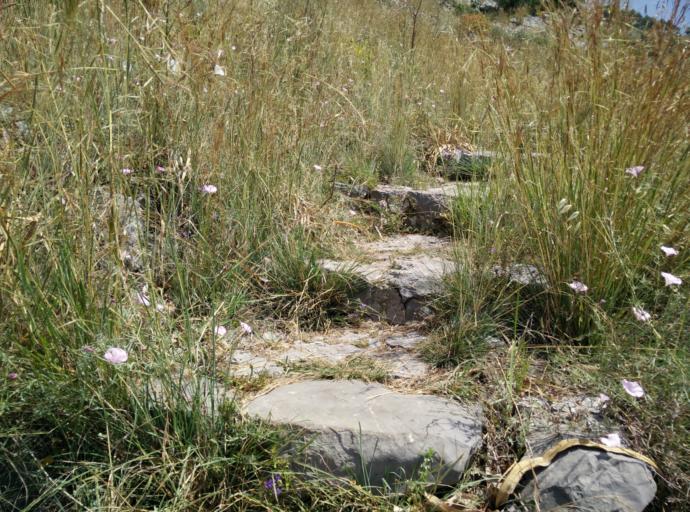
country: IT
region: Campania
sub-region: Provincia di Napoli
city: Massa Lubrense
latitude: 40.5927
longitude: 14.3799
